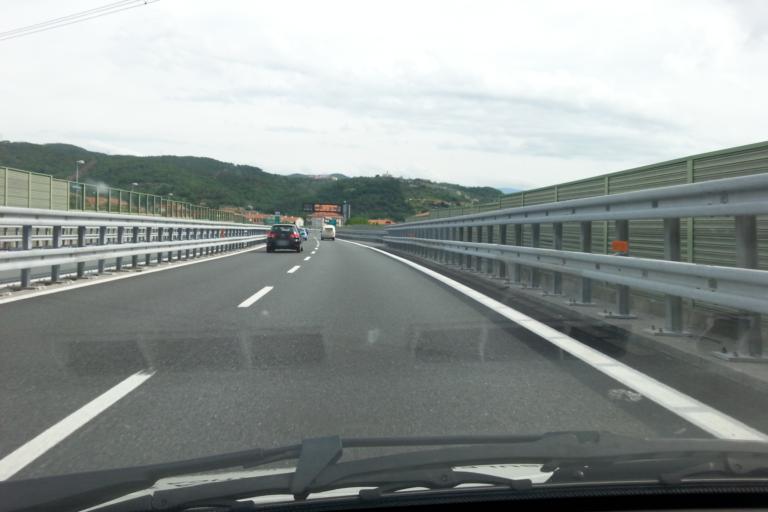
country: IT
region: Liguria
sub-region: Provincia di Savona
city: Valleggia
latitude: 44.2783
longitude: 8.4290
